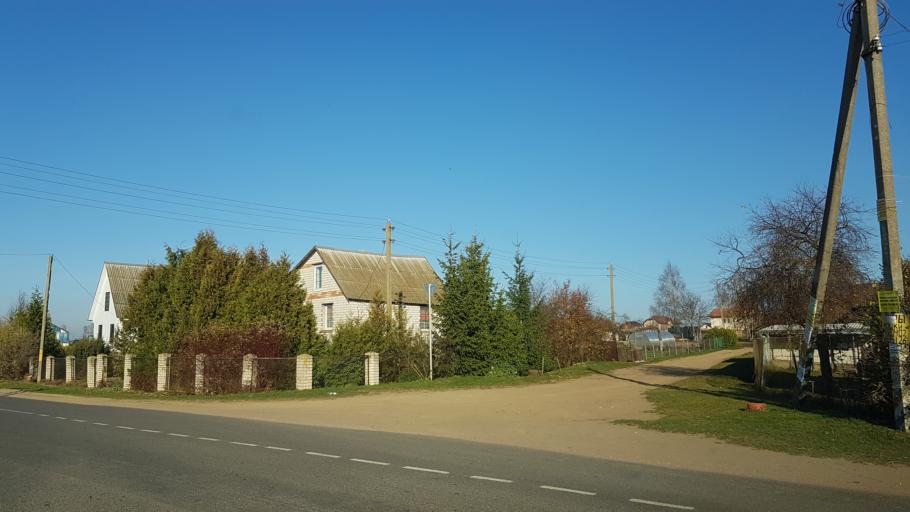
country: BY
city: Fanipol
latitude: 53.7209
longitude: 27.3142
